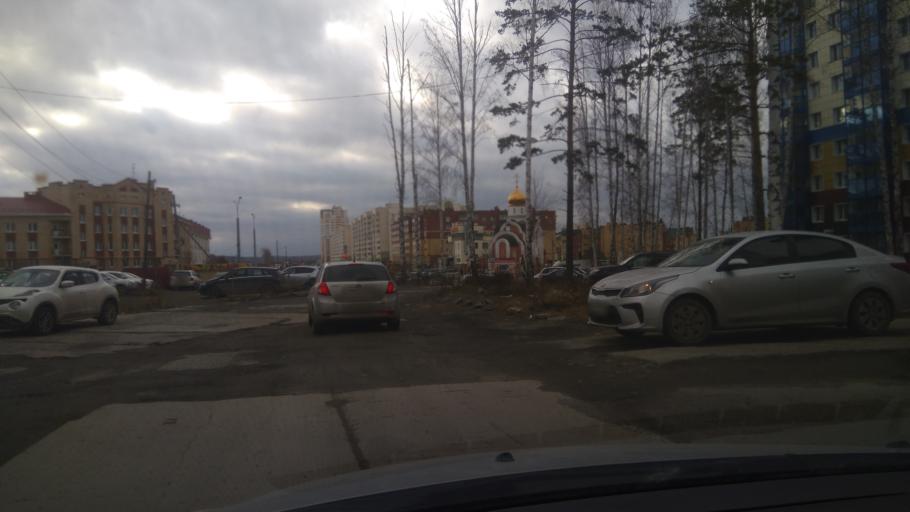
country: RU
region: Sverdlovsk
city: Sovkhoznyy
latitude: 56.7838
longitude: 60.5408
